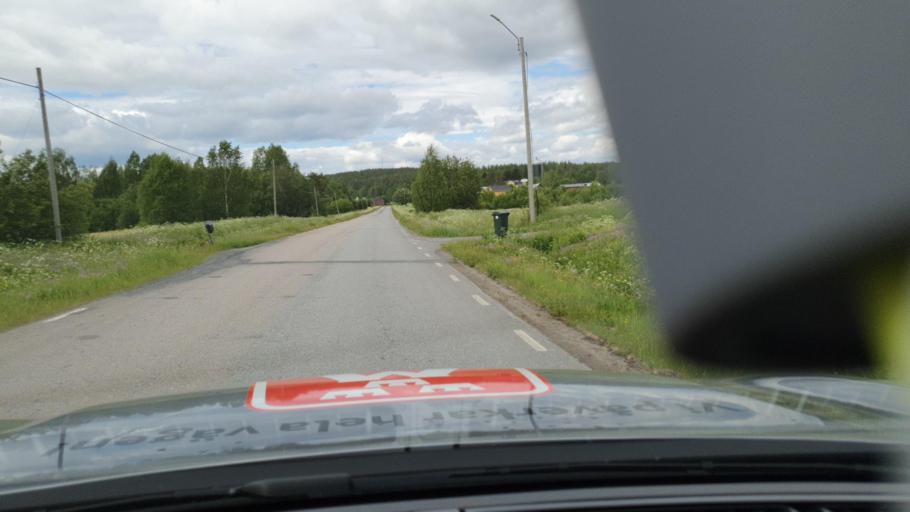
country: SE
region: Norrbotten
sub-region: Bodens Kommun
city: Saevast
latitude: 65.8668
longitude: 21.8999
